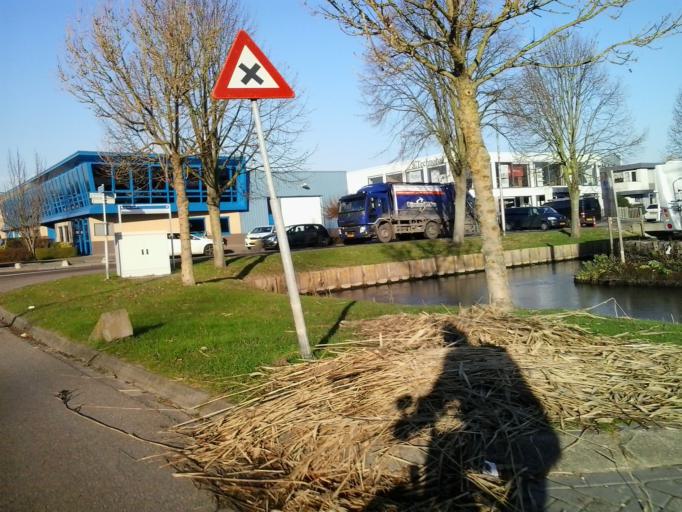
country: NL
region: South Holland
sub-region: Gemeente Lansingerland
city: Bergschenhoek
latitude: 51.9776
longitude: 4.5015
